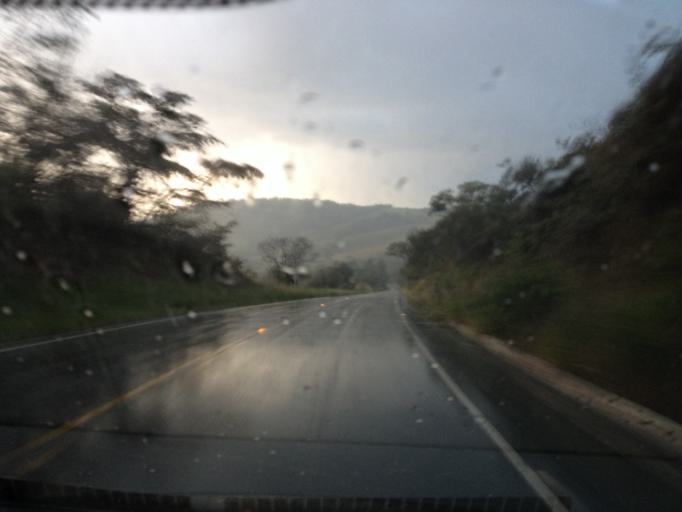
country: BR
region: Minas Gerais
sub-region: Caxambu
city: Caxambu
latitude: -21.9829
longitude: -44.9895
